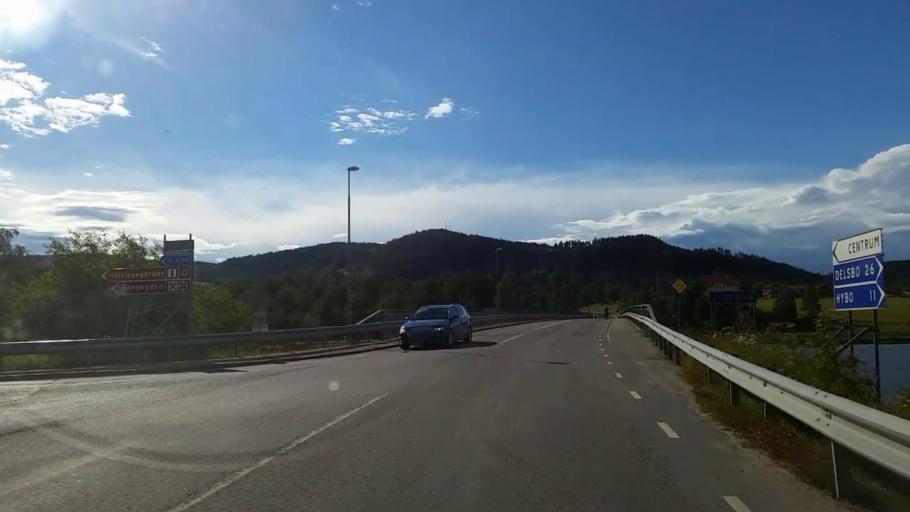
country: SE
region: Gaevleborg
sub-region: Ljusdals Kommun
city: Jaervsoe
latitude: 61.7102
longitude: 16.1861
